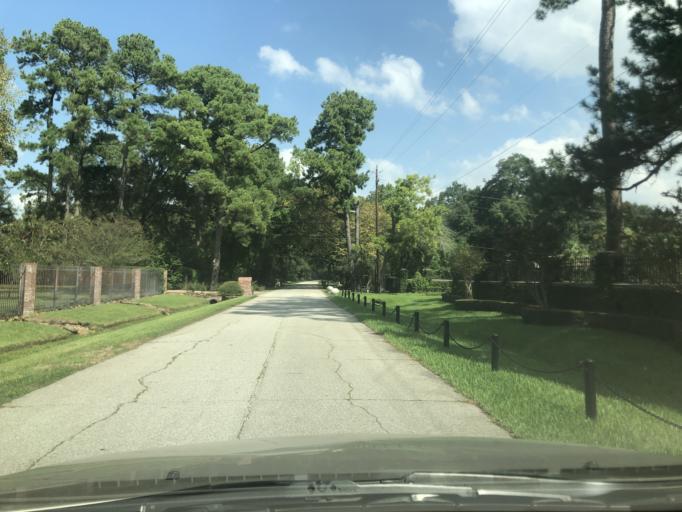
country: US
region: Texas
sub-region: Harris County
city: Bunker Hill Village
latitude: 29.7422
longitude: -95.5418
